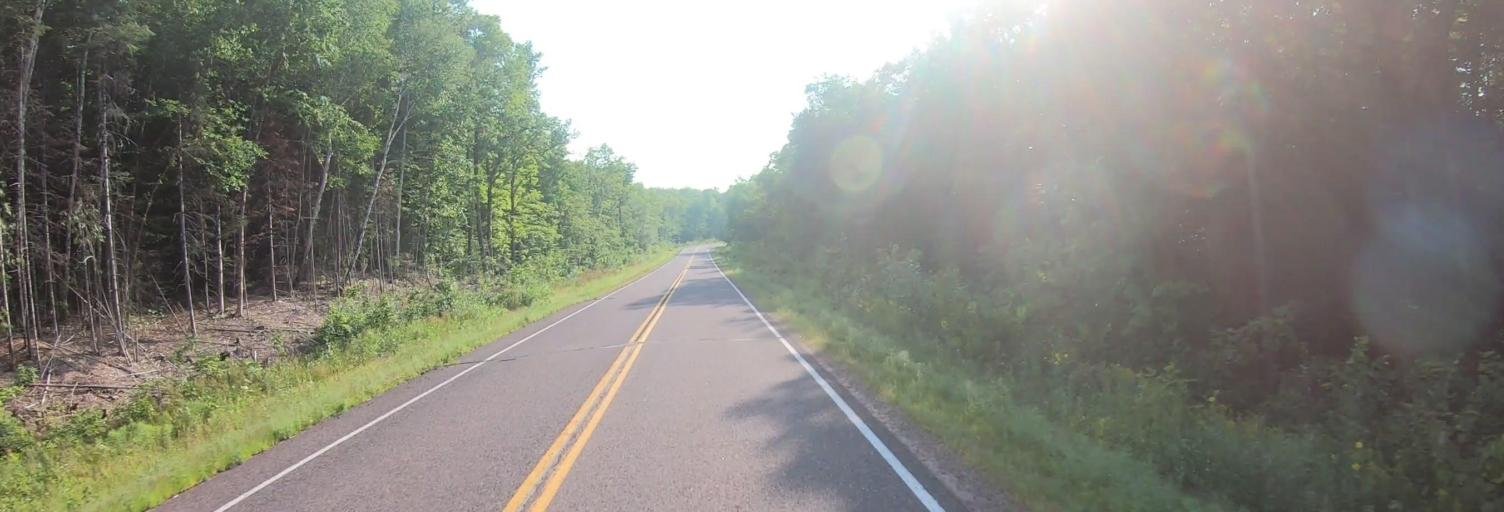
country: US
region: Wisconsin
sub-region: Ashland County
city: Ashland
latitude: 46.3032
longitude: -90.7755
